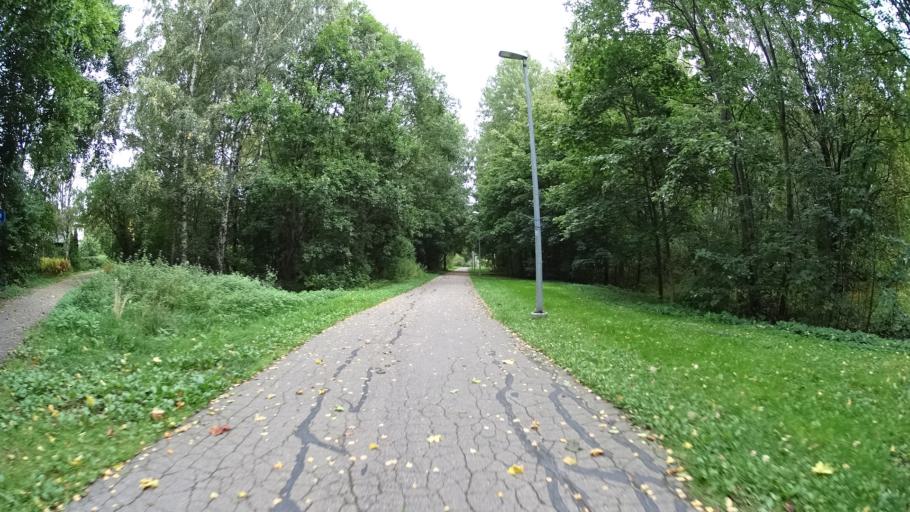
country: FI
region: Uusimaa
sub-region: Helsinki
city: Helsinki
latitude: 60.2350
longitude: 24.9685
